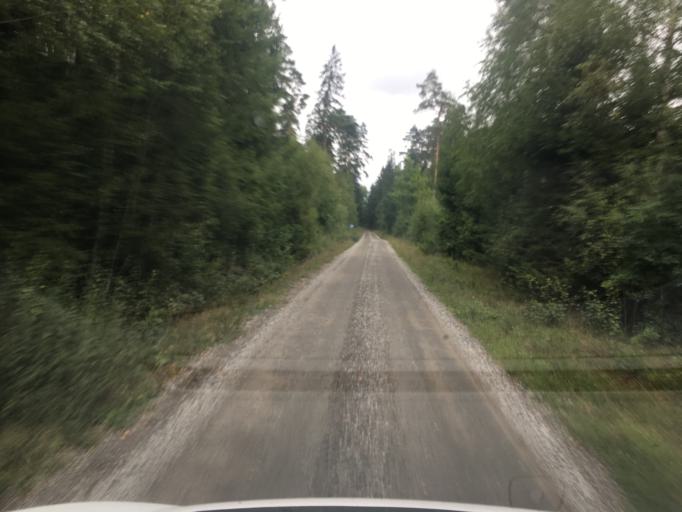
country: SE
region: Kronoberg
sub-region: Ljungby Kommun
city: Lagan
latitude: 56.9588
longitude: 14.0430
